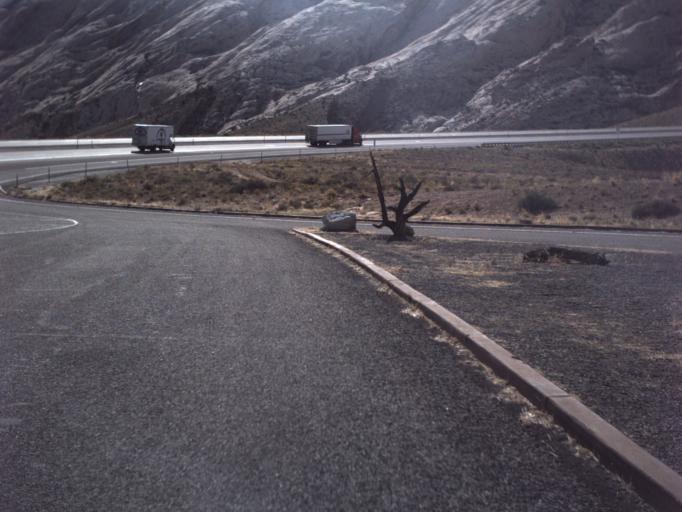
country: US
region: Utah
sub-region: Carbon County
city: East Carbon City
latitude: 38.9207
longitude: -110.4310
